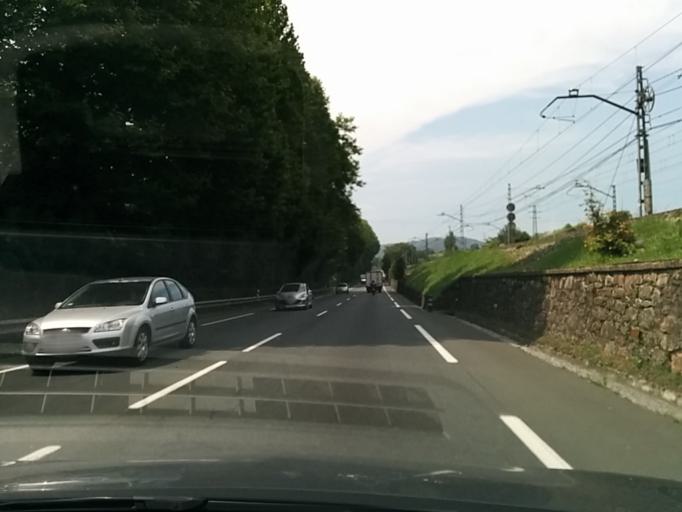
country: ES
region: Basque Country
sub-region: Provincia de Guipuzcoa
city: Lezo
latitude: 43.3249
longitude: -1.8602
